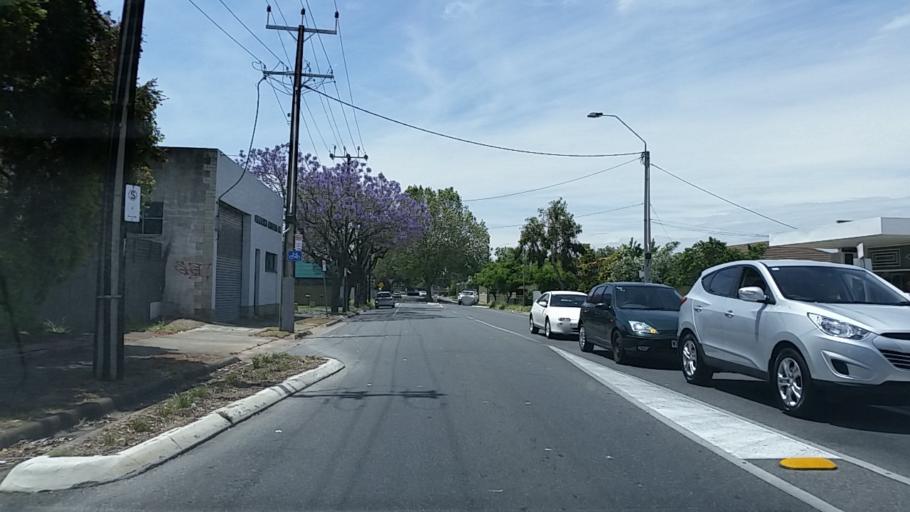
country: AU
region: South Australia
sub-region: Charles Sturt
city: Allenby Gardens
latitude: -34.8932
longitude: 138.5549
